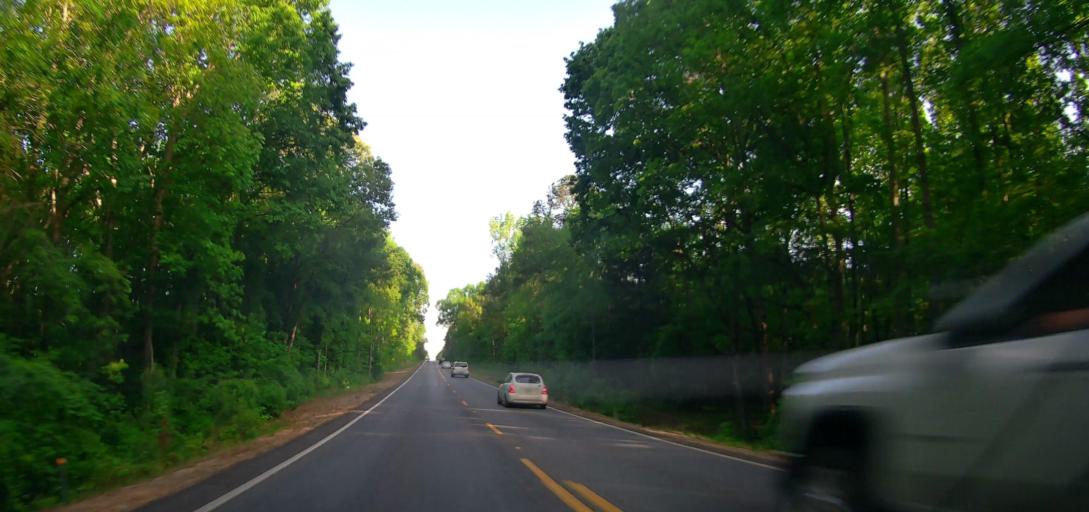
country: US
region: Georgia
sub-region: Putnam County
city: Eatonton
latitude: 33.3627
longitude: -83.5253
